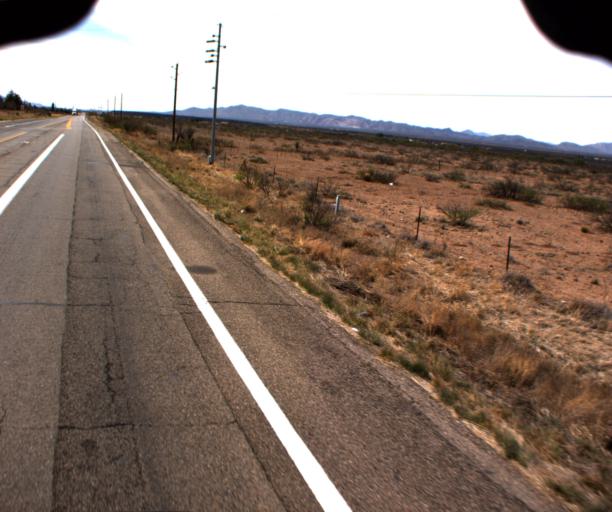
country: US
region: Arizona
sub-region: Cochise County
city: Pirtleville
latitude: 31.3724
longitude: -109.5794
